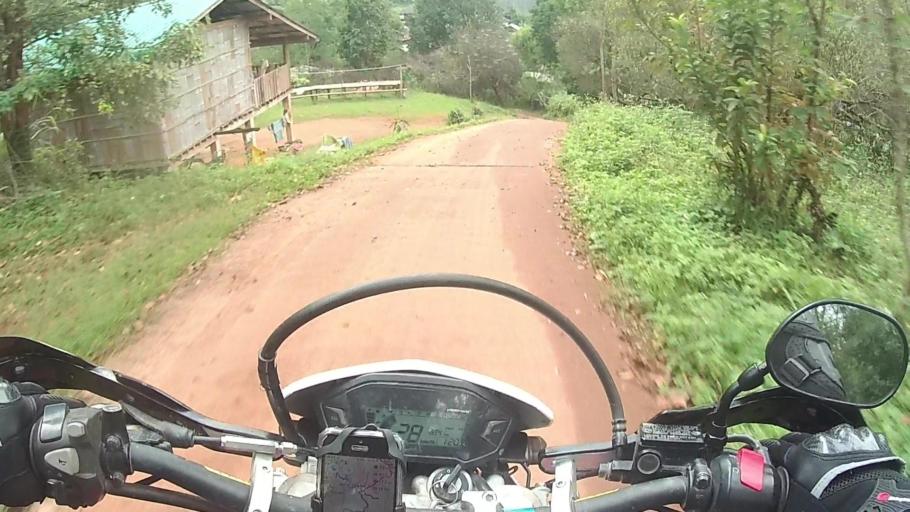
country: TH
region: Lampang
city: Wang Nuea
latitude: 19.0527
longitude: 99.4665
